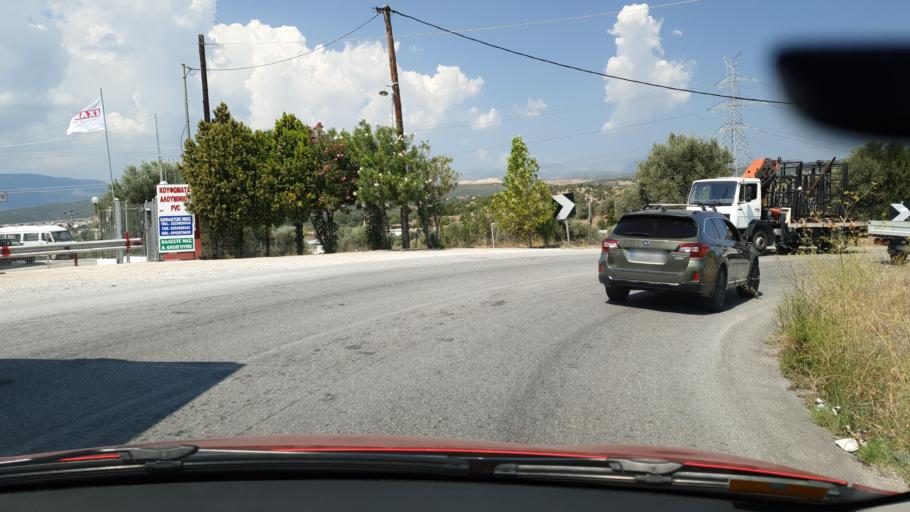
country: GR
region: Central Greece
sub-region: Nomos Evvoias
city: Aliveri
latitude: 38.3955
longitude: 24.0646
